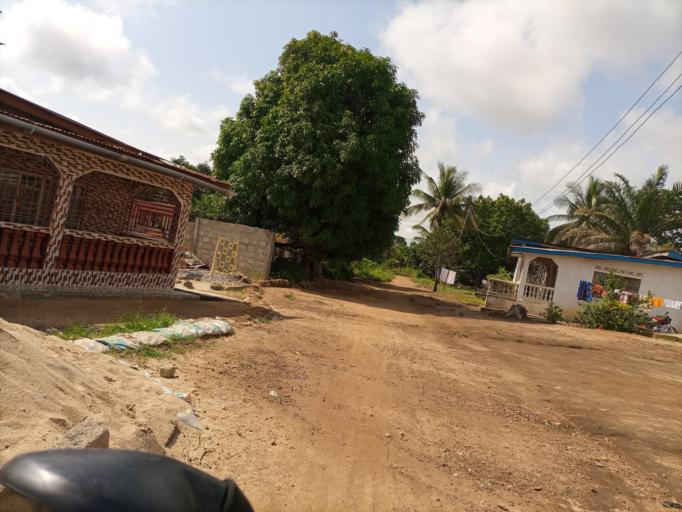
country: SL
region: Southern Province
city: Bo
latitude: 7.9672
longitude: -11.7634
